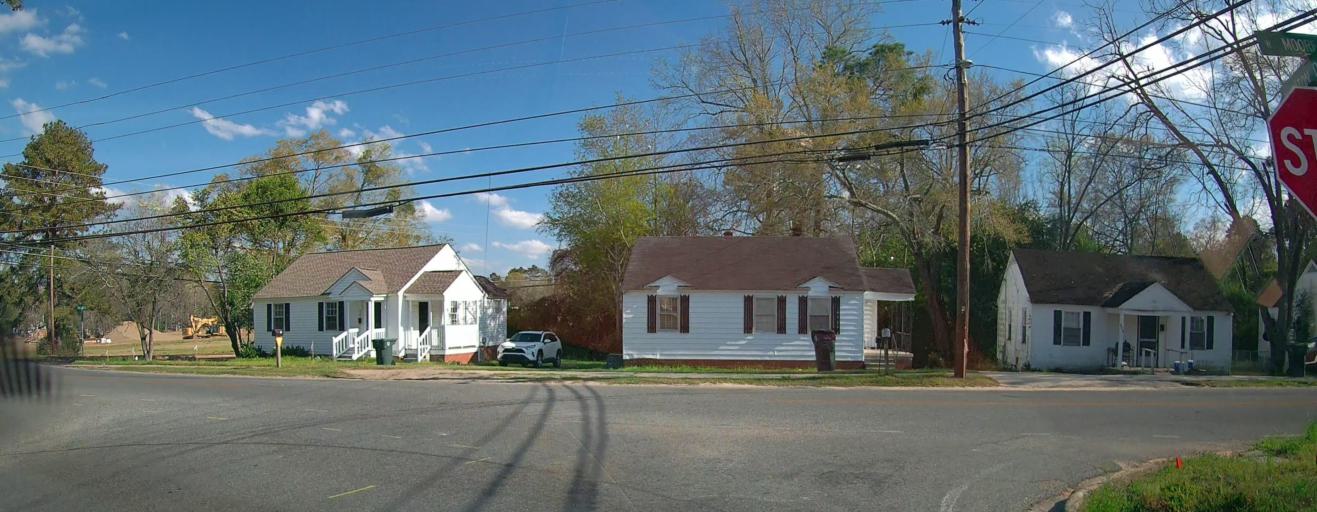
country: US
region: Georgia
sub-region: Laurens County
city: Dublin
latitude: 32.5419
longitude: -82.9177
